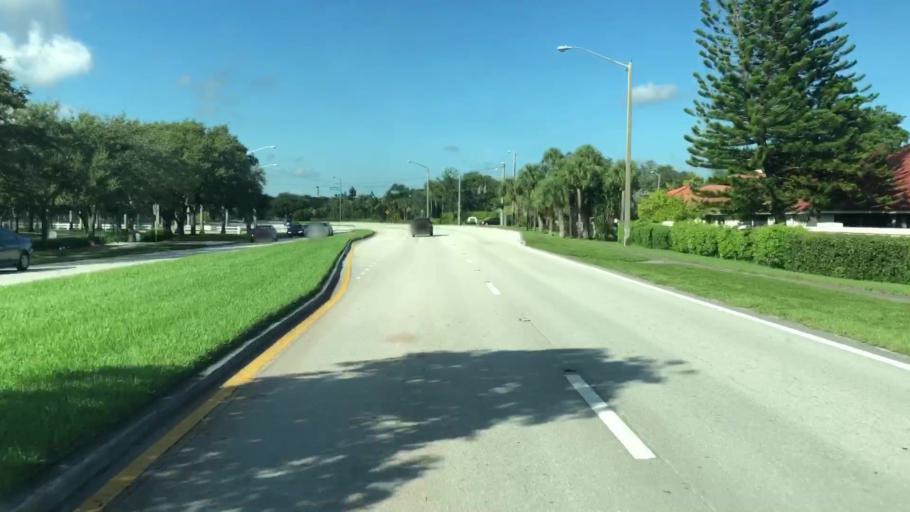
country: US
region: Florida
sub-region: Broward County
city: Coral Springs
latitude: 26.2502
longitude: -80.2675
